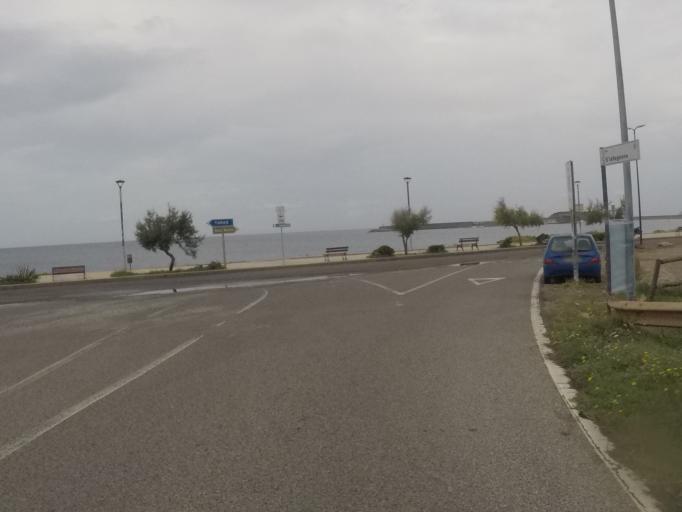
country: IT
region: Sardinia
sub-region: Provincia di Oristano
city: Bosa
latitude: 40.2839
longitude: 8.4838
